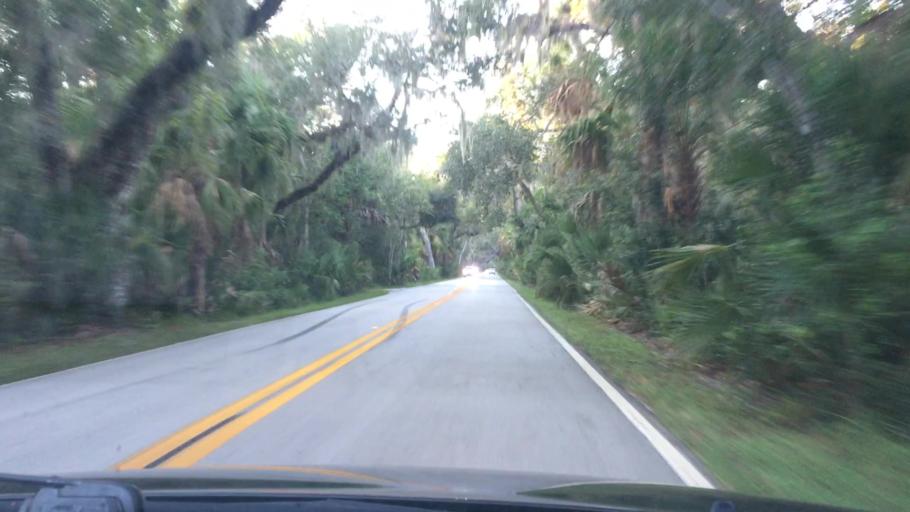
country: US
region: Florida
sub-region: Volusia County
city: Ormond-by-the-Sea
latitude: 29.3356
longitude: -81.0812
